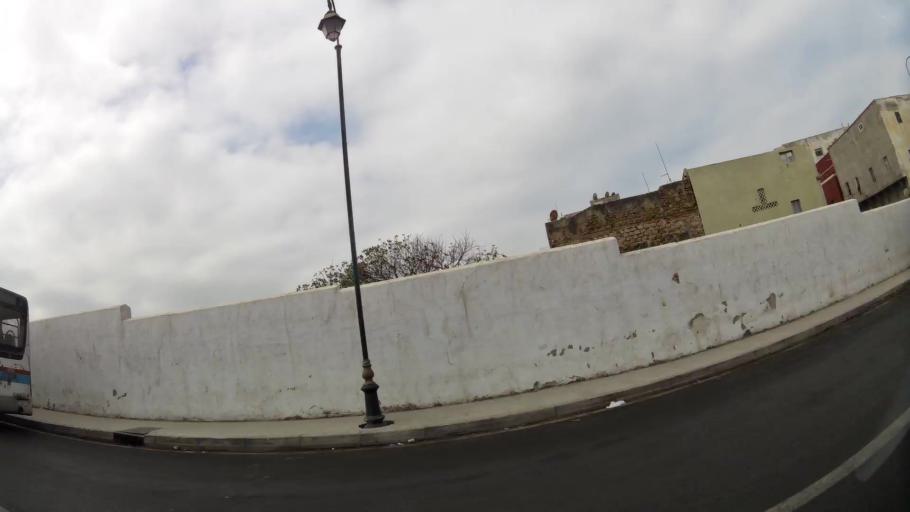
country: MA
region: Rabat-Sale-Zemmour-Zaer
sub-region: Rabat
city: Rabat
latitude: 34.0285
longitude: -6.8443
